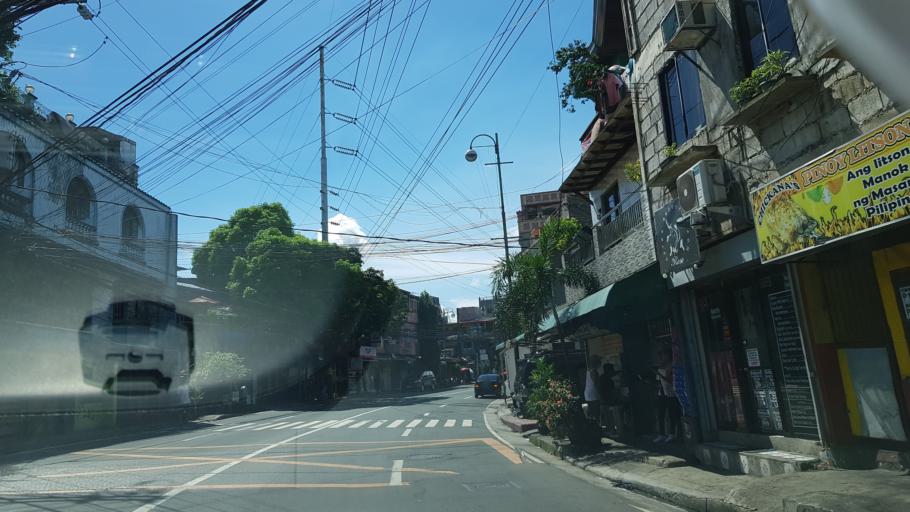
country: PH
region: Calabarzon
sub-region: Province of Rizal
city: Pateros
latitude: 14.5603
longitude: 121.0635
